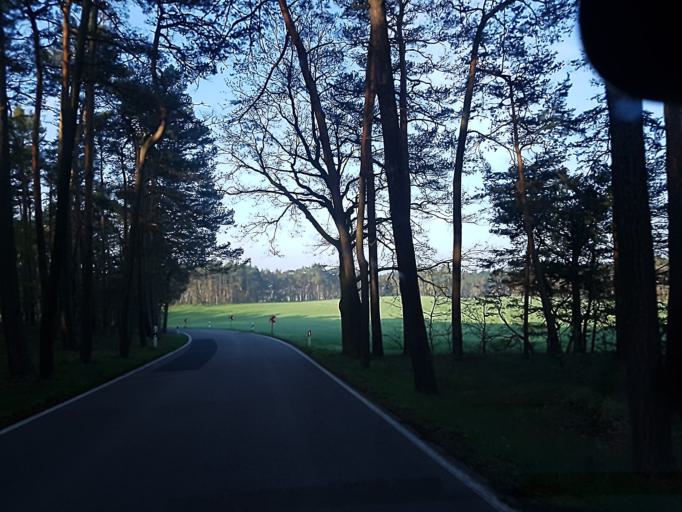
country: DE
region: Saxony
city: Cavertitz
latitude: 51.4101
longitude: 13.1404
